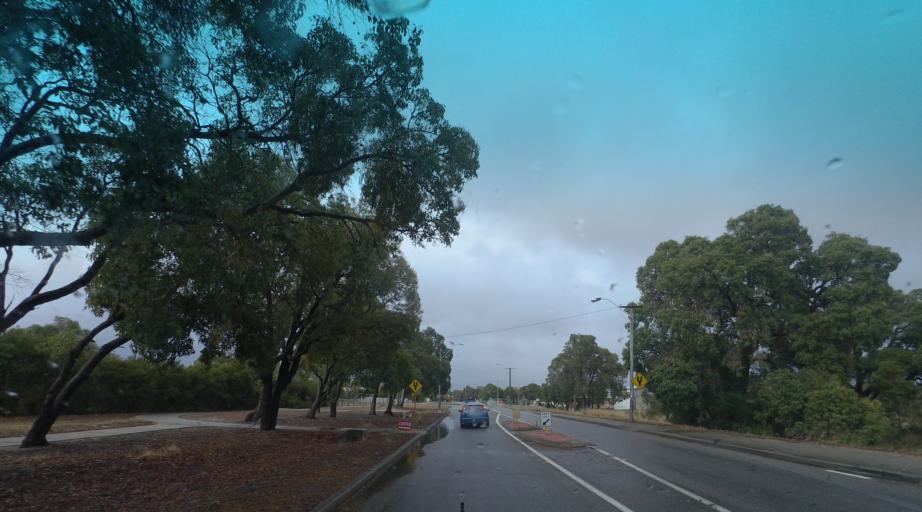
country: AU
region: Western Australia
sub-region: Serpentine-Jarrahdale
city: Byford
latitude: -32.2119
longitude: 116.0096
